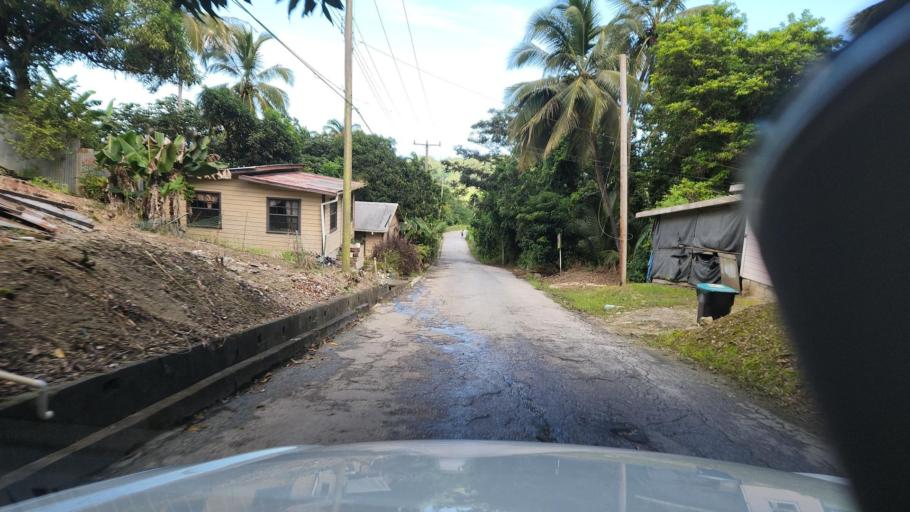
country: BB
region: Saint Thomas
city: Welchman Hall
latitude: 13.2045
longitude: -59.5589
